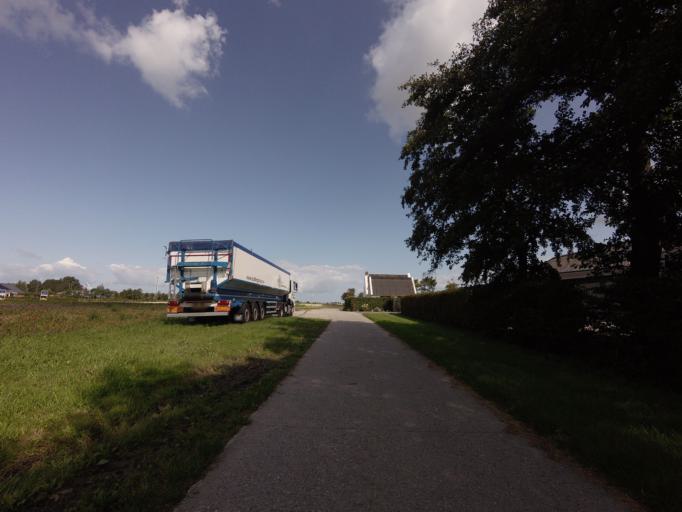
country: NL
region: Friesland
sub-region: Gemeente Het Bildt
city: Sint Jacobiparochie
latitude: 53.2729
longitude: 5.6154
